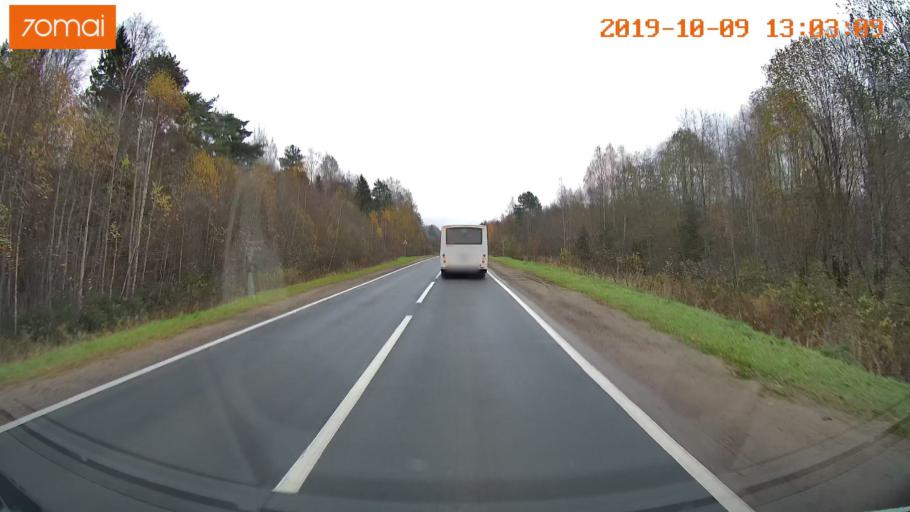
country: RU
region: Jaroslavl
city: Lyubim
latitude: 58.3597
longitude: 40.5188
